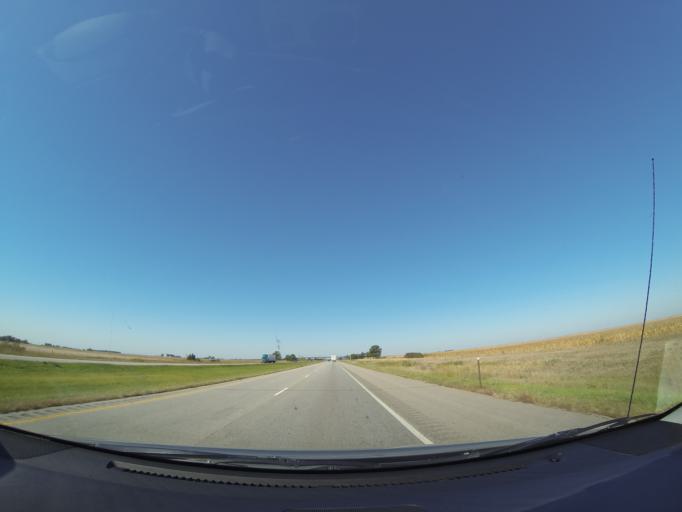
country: US
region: Nebraska
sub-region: Seward County
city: Seward
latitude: 40.8225
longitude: -97.1522
